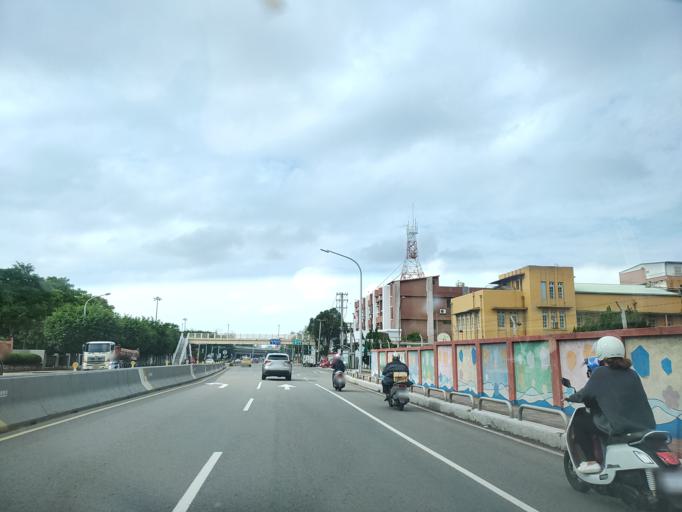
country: TW
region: Taiwan
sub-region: Hsinchu
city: Hsinchu
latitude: 24.7884
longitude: 121.0086
